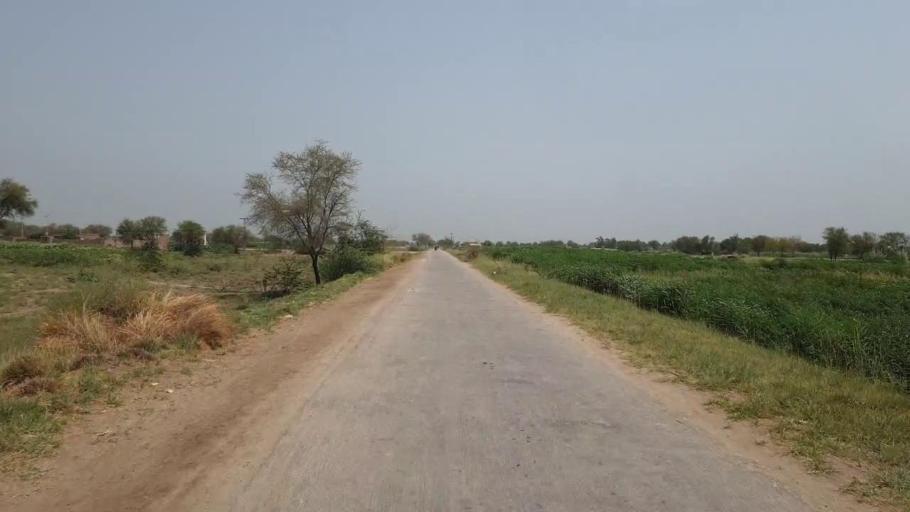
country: PK
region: Sindh
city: Nawabshah
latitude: 26.2561
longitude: 68.3207
